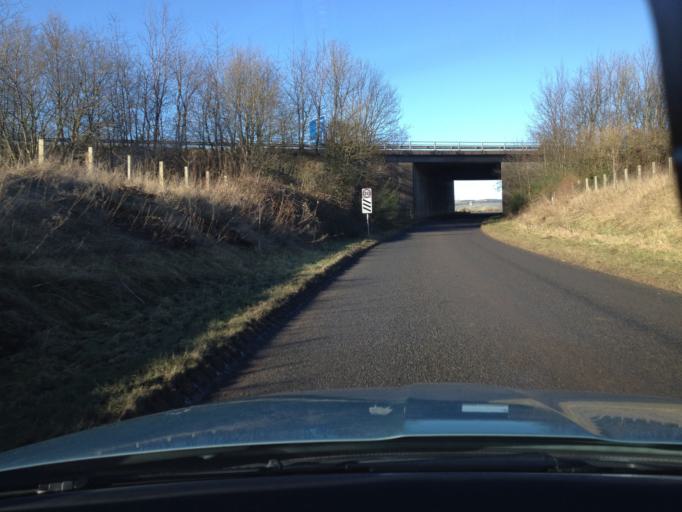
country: GB
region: Scotland
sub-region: Perth and Kinross
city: Bridge of Earn
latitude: 56.3364
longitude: -3.3980
